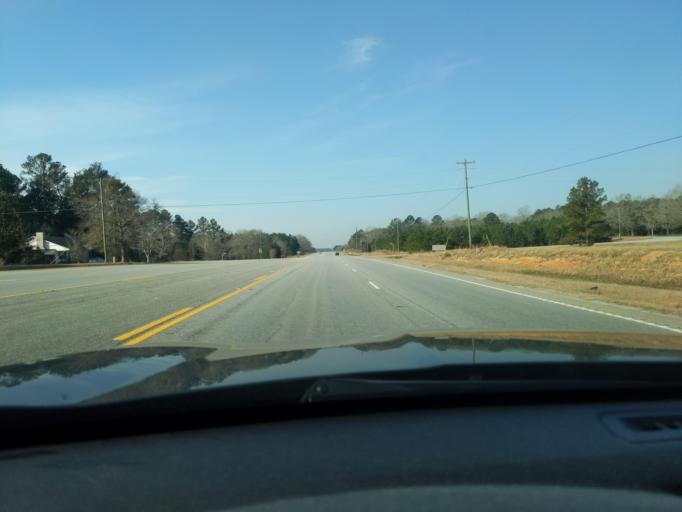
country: US
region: South Carolina
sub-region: Abbeville County
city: Abbeville
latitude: 34.1341
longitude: -82.4159
